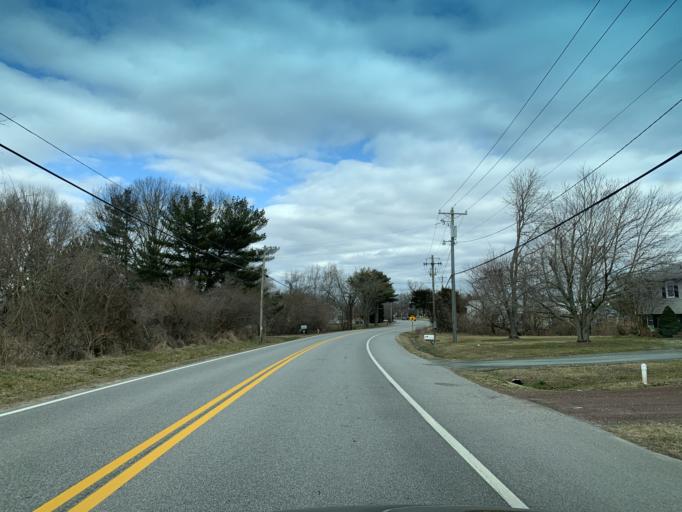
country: US
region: Maryland
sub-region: Queen Anne's County
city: Centreville
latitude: 39.0353
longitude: -76.0770
